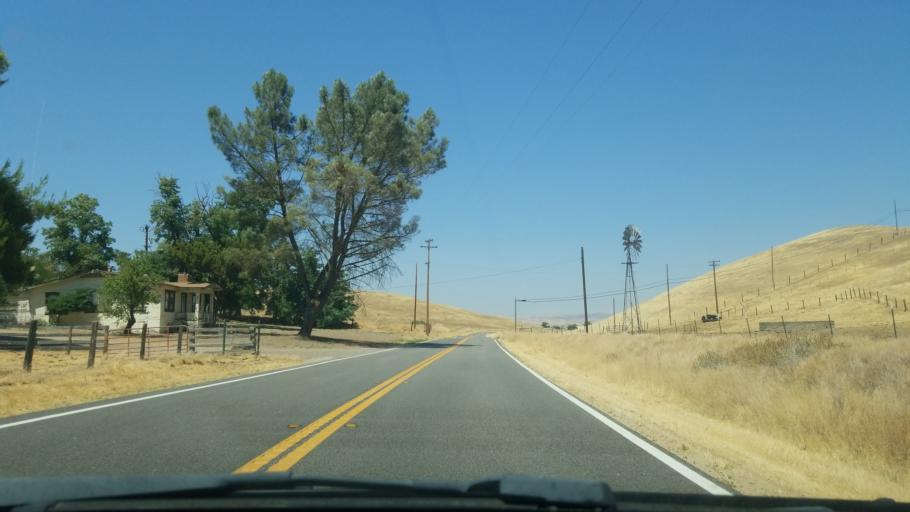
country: US
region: California
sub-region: San Luis Obispo County
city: Shandon
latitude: 35.6146
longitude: -120.4051
